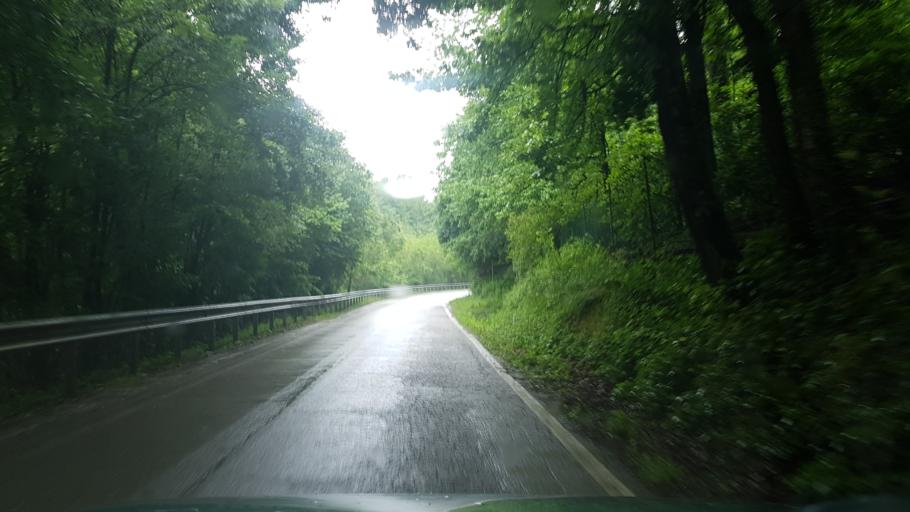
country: IT
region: Friuli Venezia Giulia
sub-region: Provincia di Gorizia
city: Gorizia
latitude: 45.9563
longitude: 13.6049
